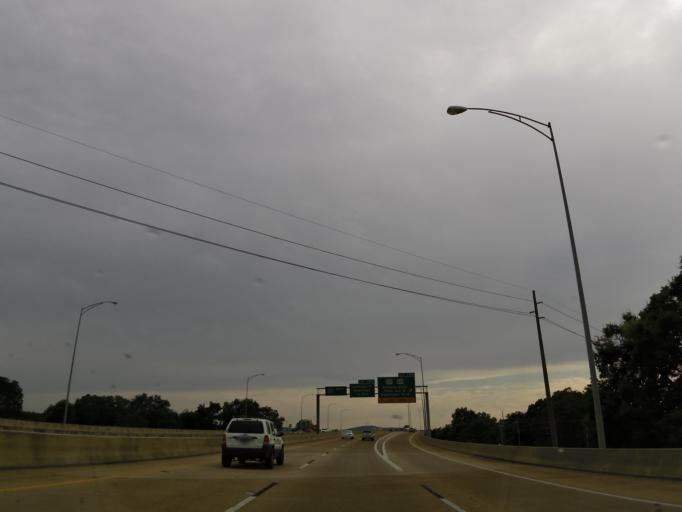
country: US
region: Alabama
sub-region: Madison County
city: Huntsville
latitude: 34.7434
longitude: -86.5814
